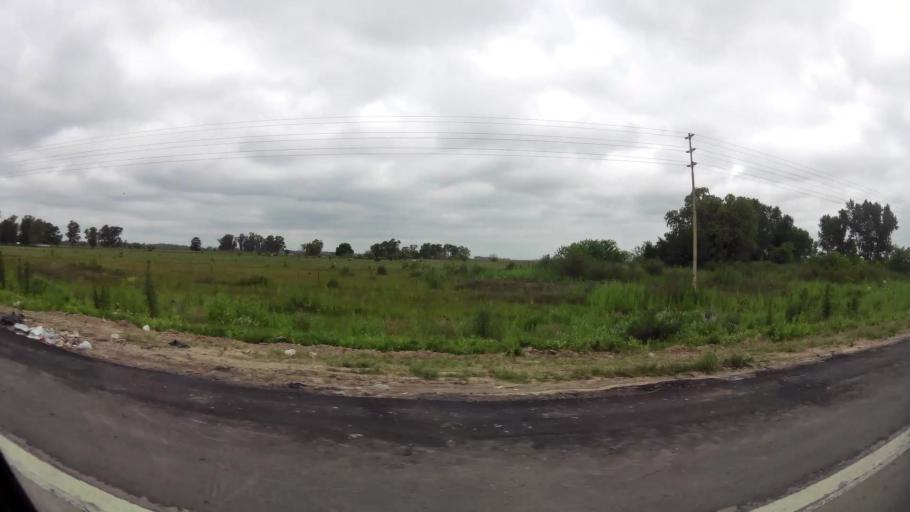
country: AR
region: Buenos Aires
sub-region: Partido de San Vicente
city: San Vicente
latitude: -35.0541
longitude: -58.4394
